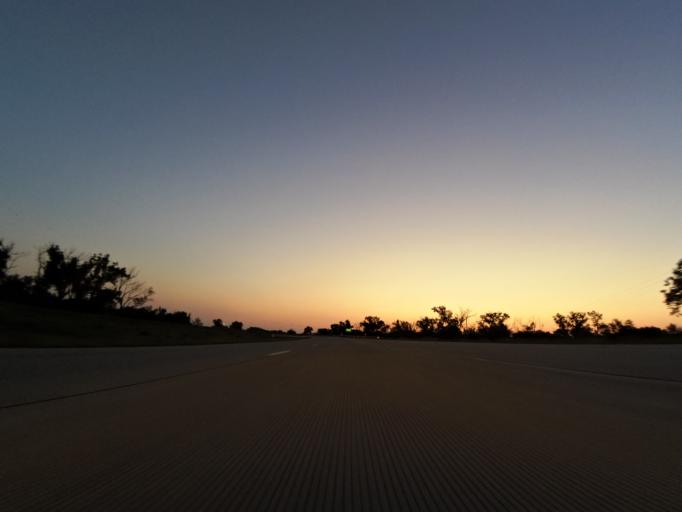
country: US
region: Kansas
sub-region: Reno County
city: South Hutchinson
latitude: 38.0146
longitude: -97.9156
